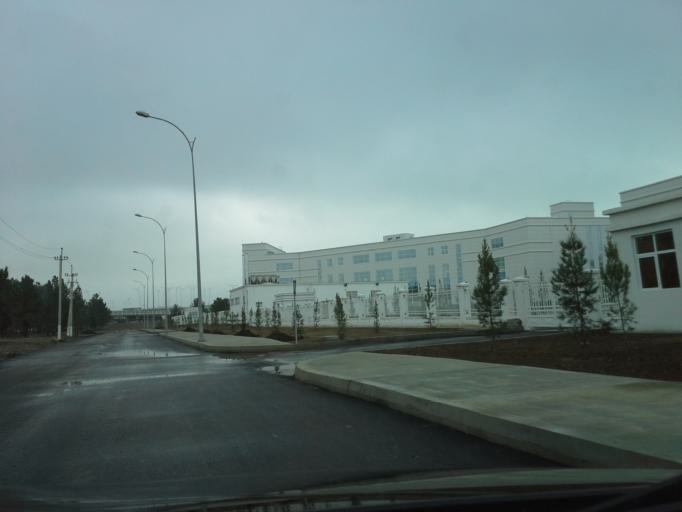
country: TM
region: Ahal
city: Ashgabat
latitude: 37.9639
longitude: 58.4161
